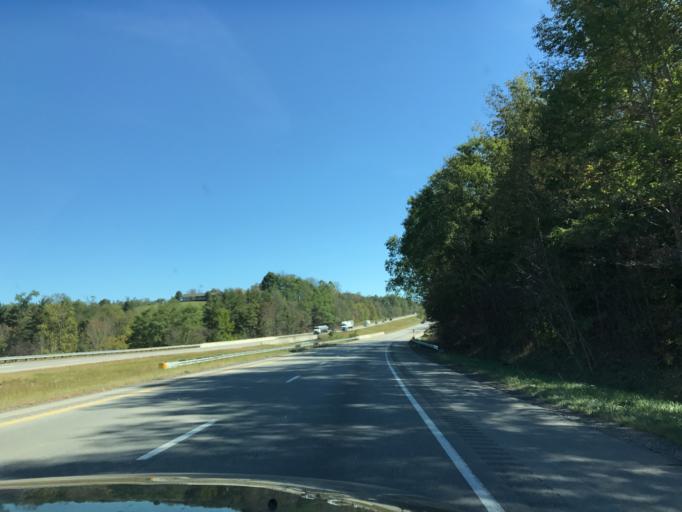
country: US
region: Ohio
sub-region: Muskingum County
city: Zanesville
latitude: 39.9532
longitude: -82.1912
